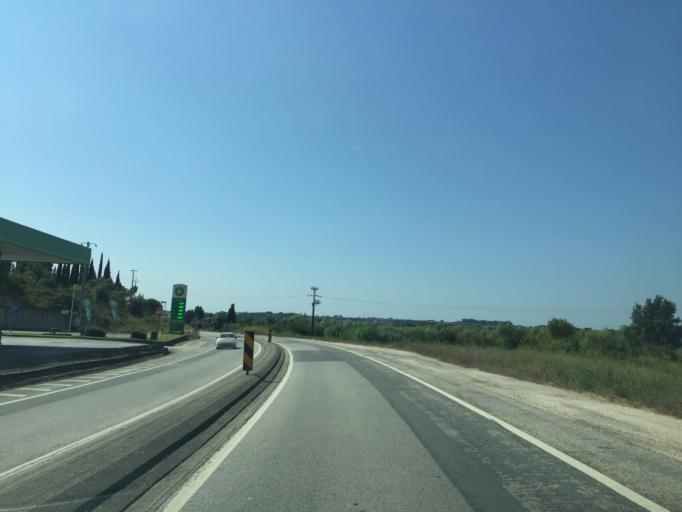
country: PT
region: Aveiro
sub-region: Mealhada
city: Mealhada
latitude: 40.3689
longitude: -8.4608
